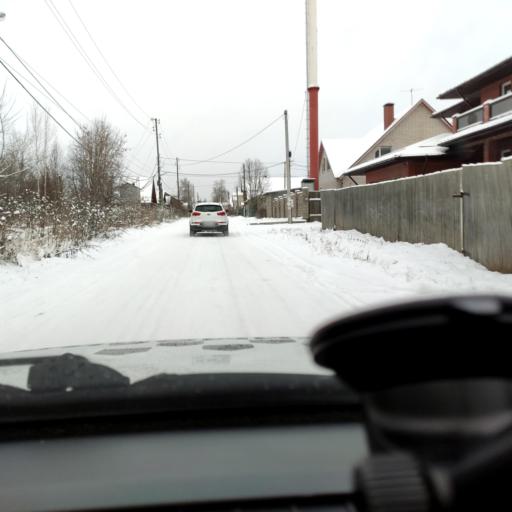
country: RU
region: Perm
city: Perm
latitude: 58.0586
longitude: 56.3631
